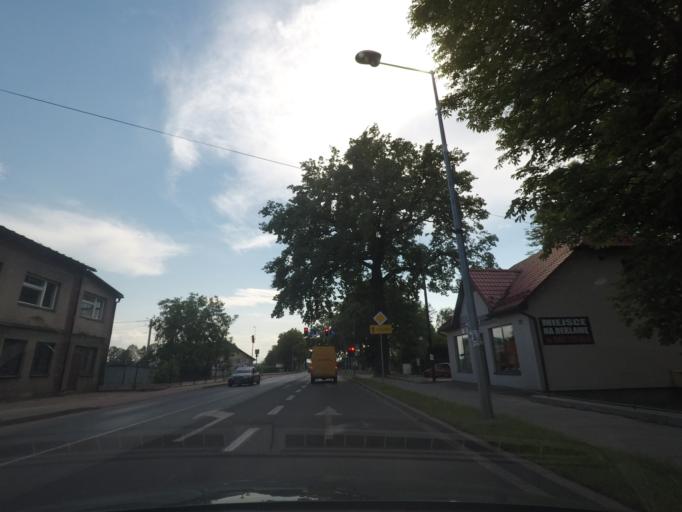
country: PL
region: Lesser Poland Voivodeship
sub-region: Powiat oswiecimski
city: Brzeszcze
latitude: 49.9840
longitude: 19.1553
